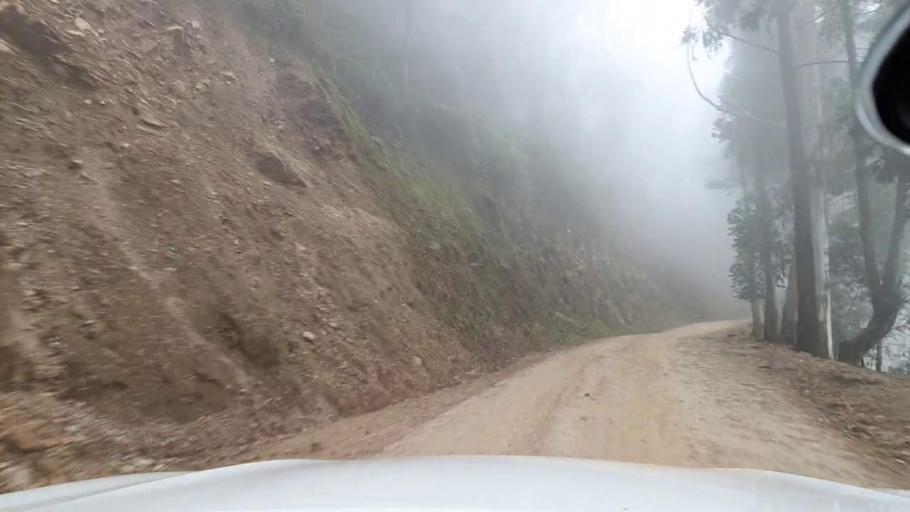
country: RW
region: Western Province
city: Cyangugu
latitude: -2.5881
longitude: 29.1885
